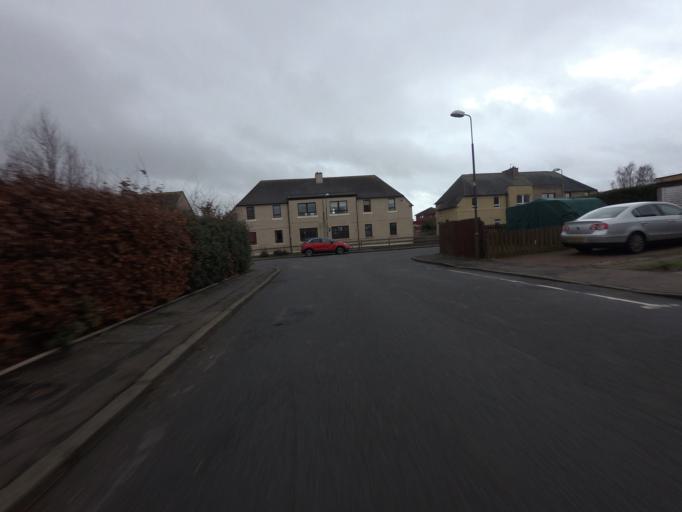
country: GB
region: Scotland
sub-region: West Lothian
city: Livingston
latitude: 55.9005
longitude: -3.5615
